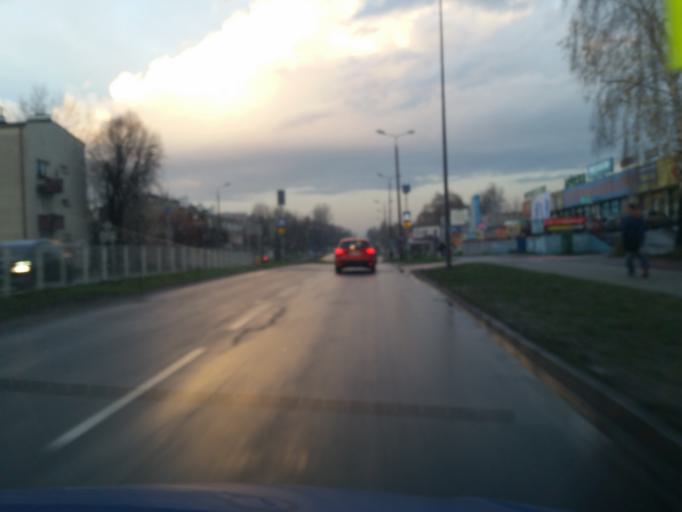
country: PL
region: Silesian Voivodeship
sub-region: Dabrowa Gornicza
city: Dabrowa Gornicza
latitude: 50.3044
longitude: 19.1888
